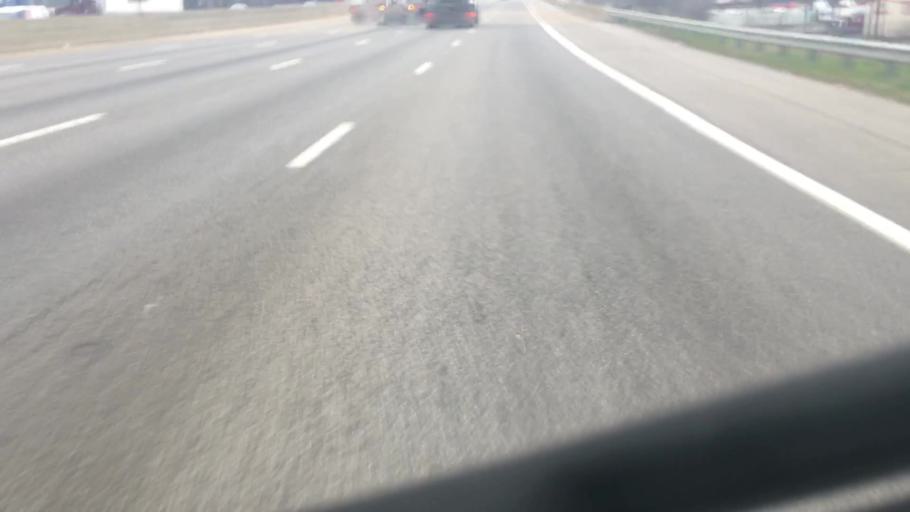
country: US
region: Alabama
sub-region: Jefferson County
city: Birmingham
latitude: 33.5439
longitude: -86.8265
